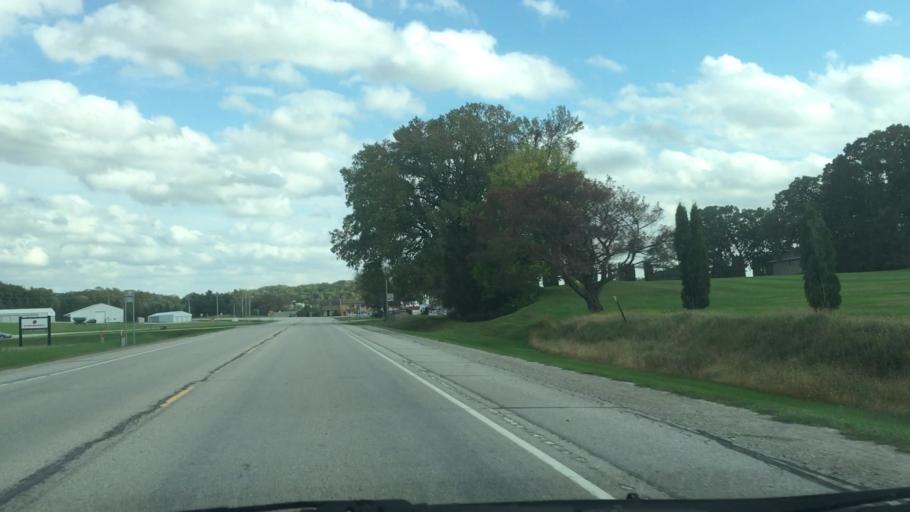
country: US
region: Minnesota
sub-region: Fillmore County
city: Chatfield
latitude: 43.8354
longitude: -92.1689
